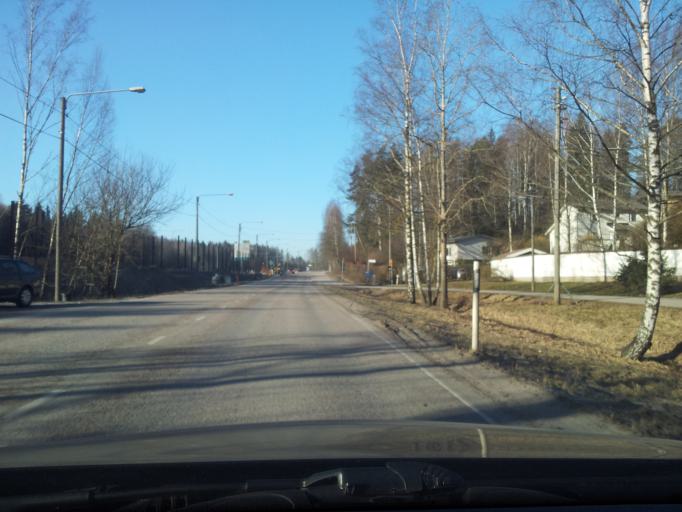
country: FI
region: Uusimaa
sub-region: Helsinki
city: Espoo
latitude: 60.1576
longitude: 24.6870
